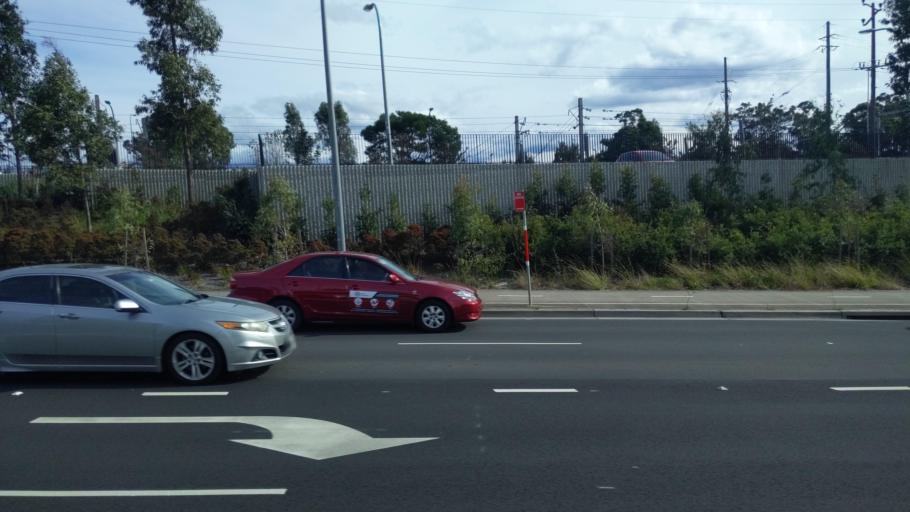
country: AU
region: New South Wales
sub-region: Blacktown
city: Riverstone
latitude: -33.7023
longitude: 150.8737
